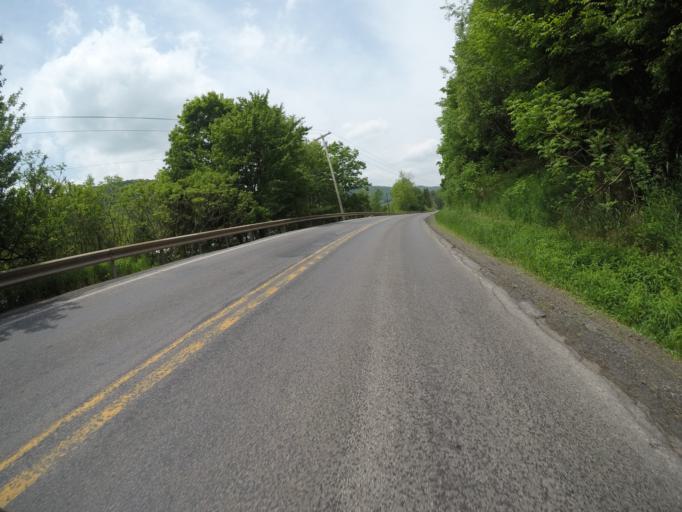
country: US
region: New York
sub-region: Delaware County
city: Delhi
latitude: 42.2595
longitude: -74.7750
